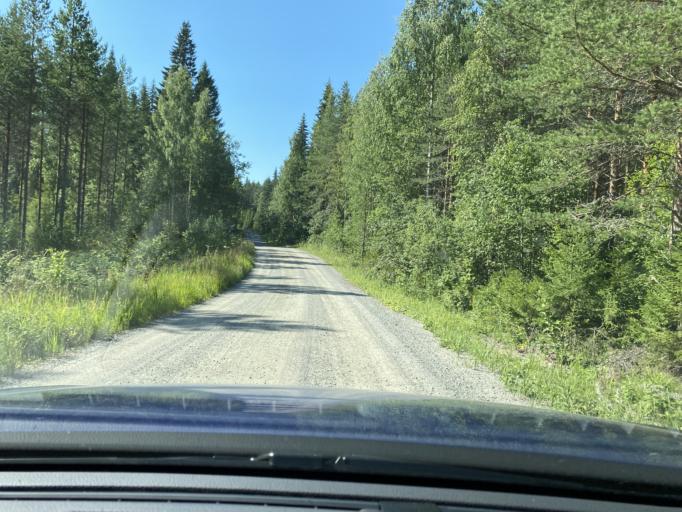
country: FI
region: Central Finland
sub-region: Jyvaeskylae
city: Korpilahti
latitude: 61.8700
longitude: 25.4027
